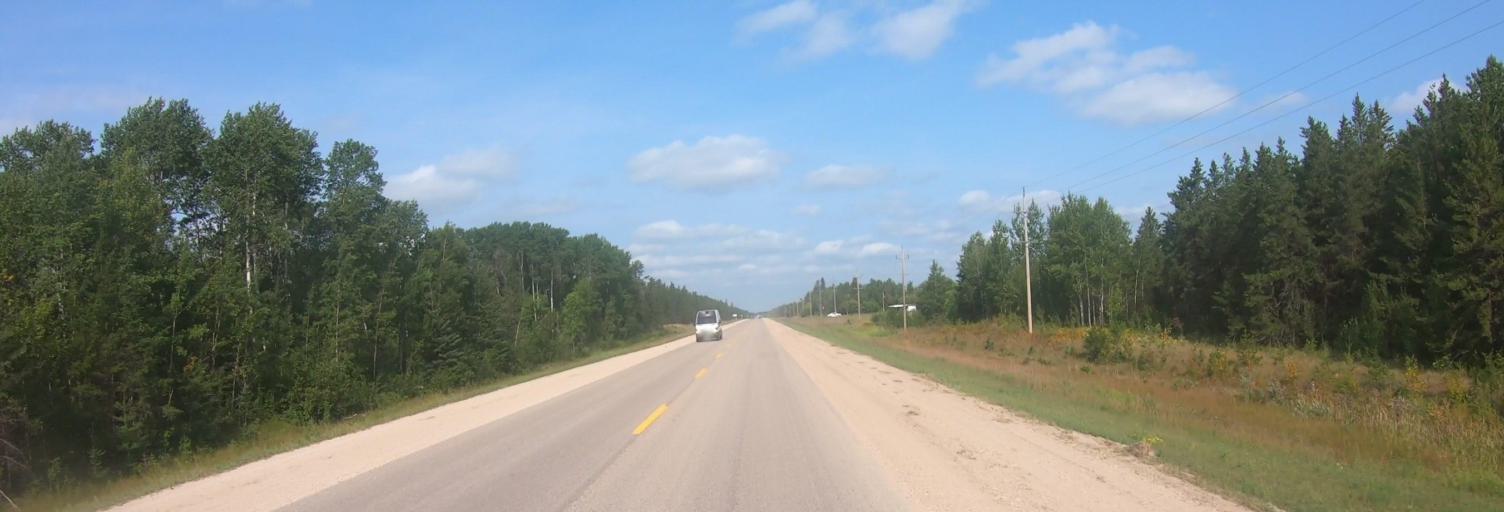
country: CA
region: Manitoba
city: La Broquerie
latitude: 49.1877
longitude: -96.2511
